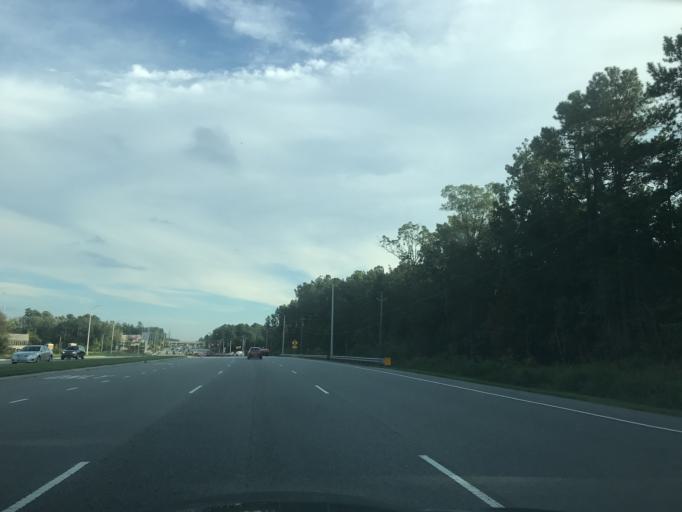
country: US
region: North Carolina
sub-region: Wake County
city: Green Level
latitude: 35.8487
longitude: -78.8932
